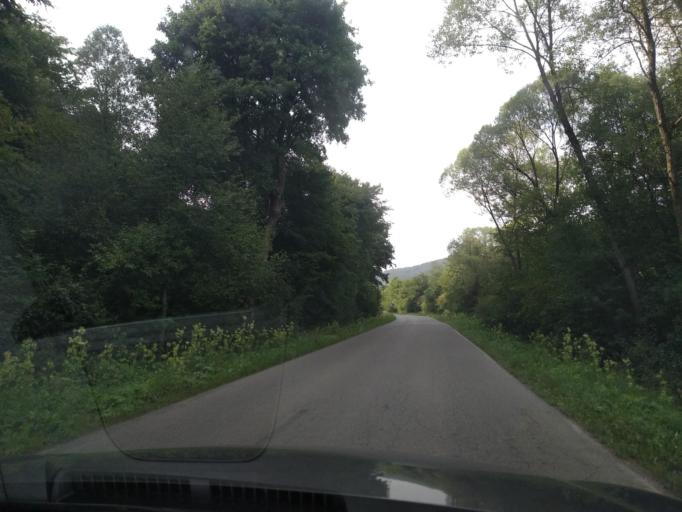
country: PL
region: Subcarpathian Voivodeship
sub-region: Powiat sanocki
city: Tyrawa Woloska
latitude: 49.5839
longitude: 22.3458
